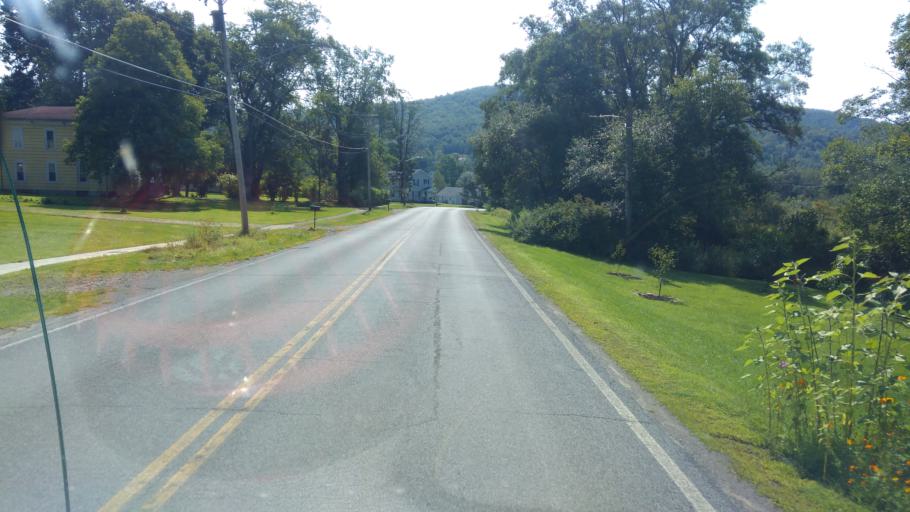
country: US
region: New York
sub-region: Allegany County
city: Bolivar
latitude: 42.0934
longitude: -78.1571
